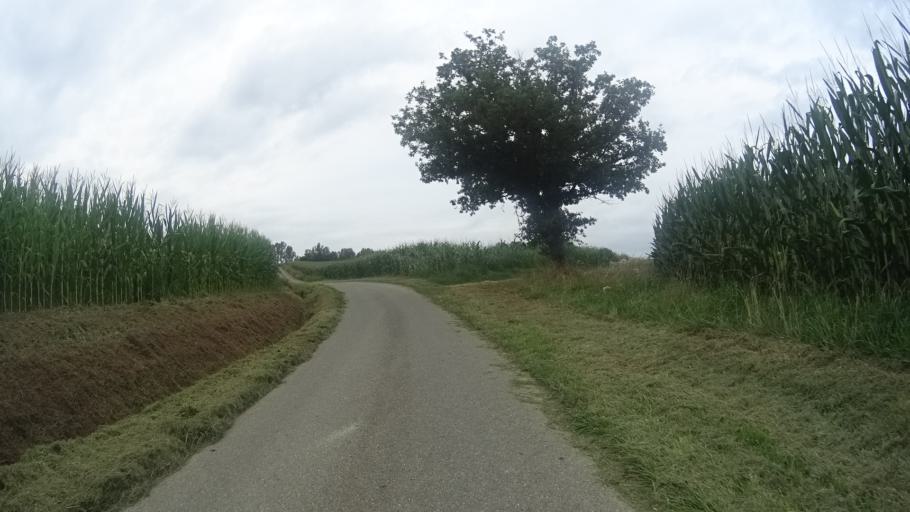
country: FR
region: Aquitaine
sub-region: Departement des Pyrenees-Atlantiques
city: Orthez
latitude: 43.4844
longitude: -0.7083
